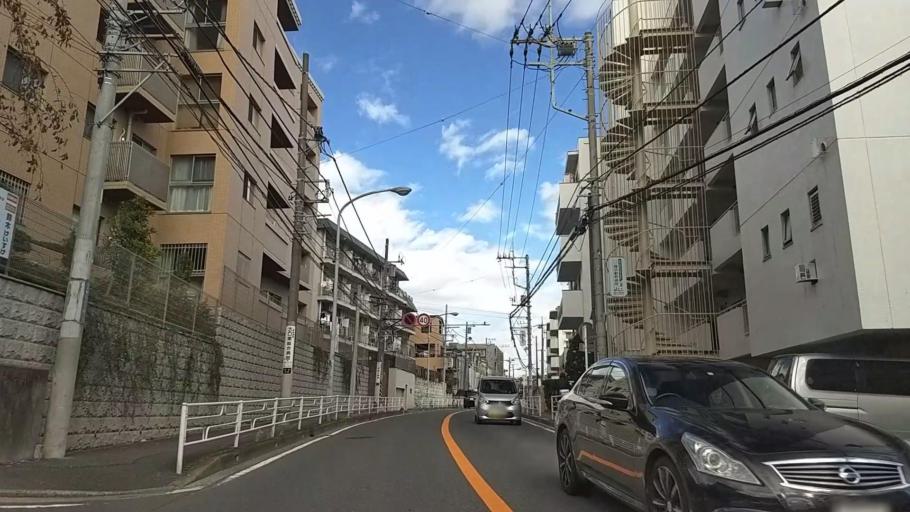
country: JP
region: Kanagawa
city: Yokohama
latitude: 35.5023
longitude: 139.6373
